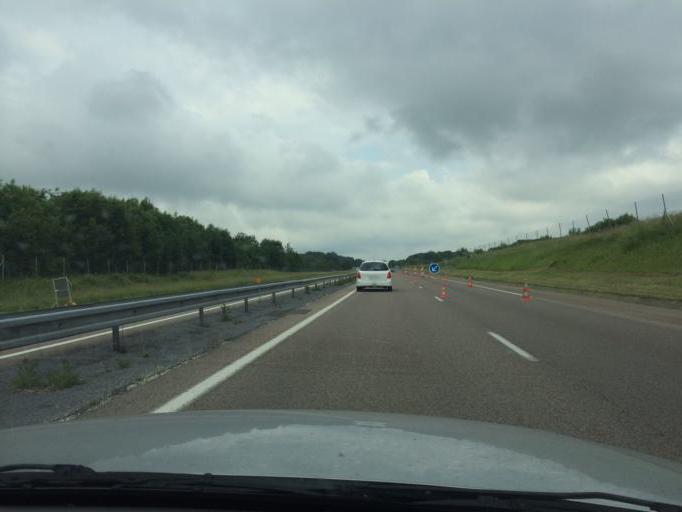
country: FR
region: Picardie
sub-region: Departement de l'Aisne
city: Brasles
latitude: 49.0980
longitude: 3.4436
